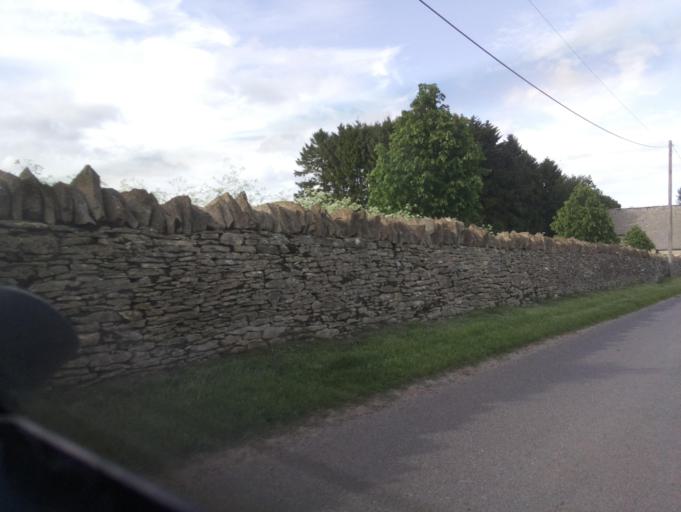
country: GB
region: England
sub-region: Gloucestershire
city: Westfield
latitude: 51.8808
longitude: -1.8923
